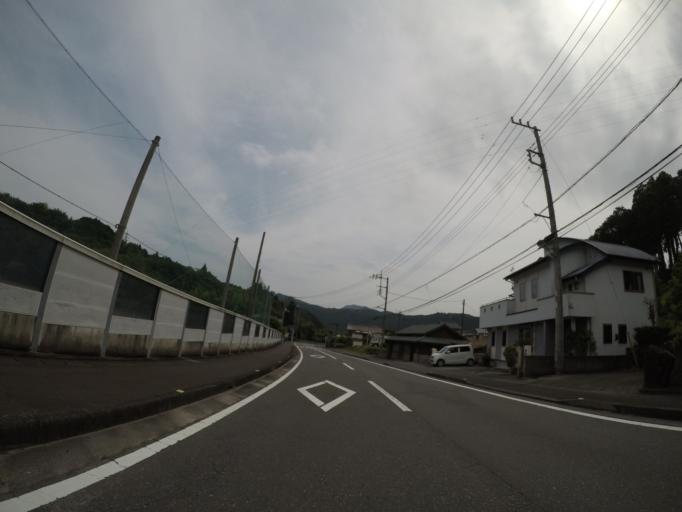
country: JP
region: Shizuoka
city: Fujinomiya
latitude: 35.2036
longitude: 138.5653
